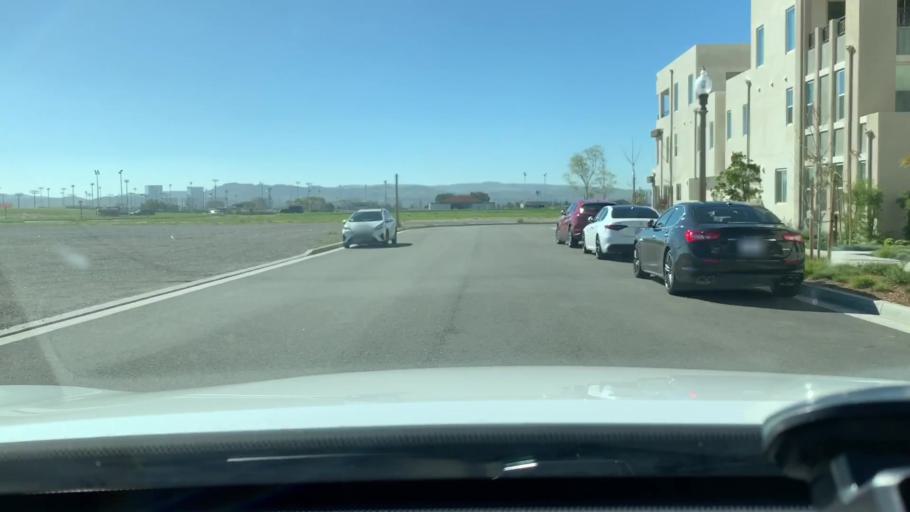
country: US
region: California
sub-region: Orange County
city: Lake Forest
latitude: 33.6797
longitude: -117.7362
